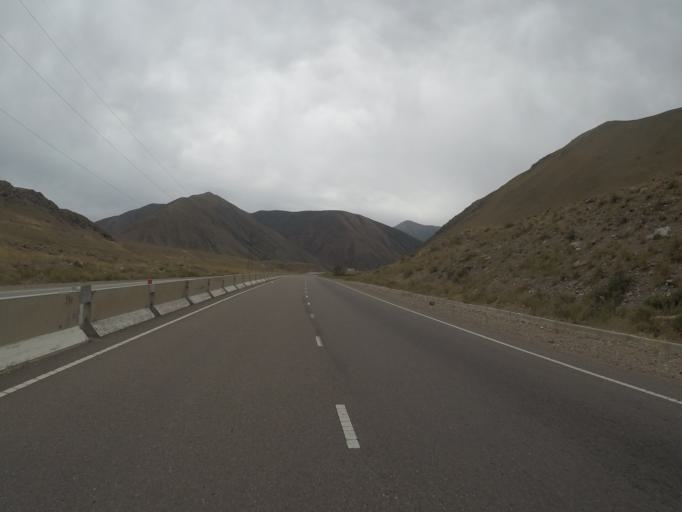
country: KG
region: Chuy
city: Bystrovka
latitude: 42.6894
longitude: 75.8836
